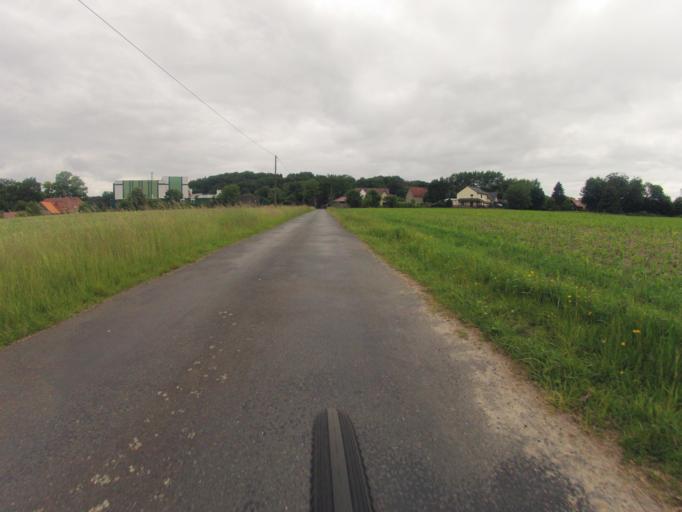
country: DE
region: North Rhine-Westphalia
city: Ibbenburen
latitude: 52.2450
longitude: 7.7422
